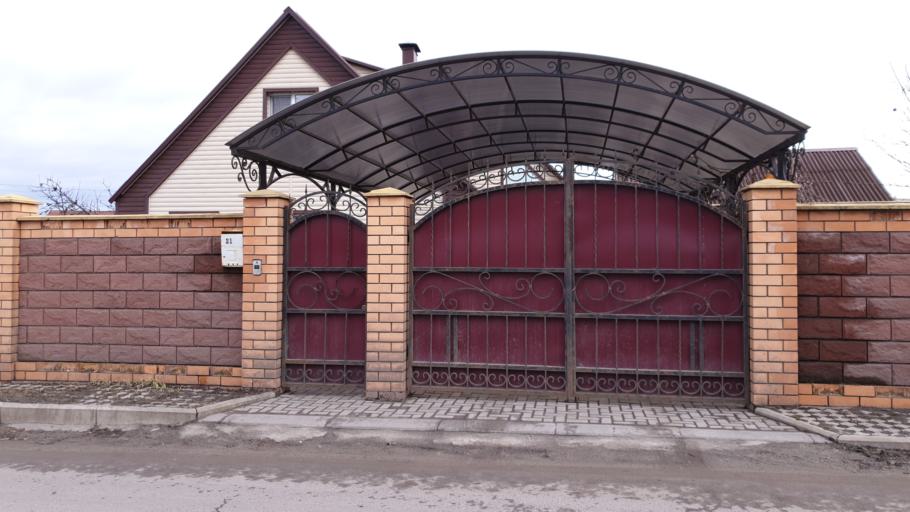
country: RU
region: Kursk
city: Voroshnevo
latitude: 51.6697
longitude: 36.0947
